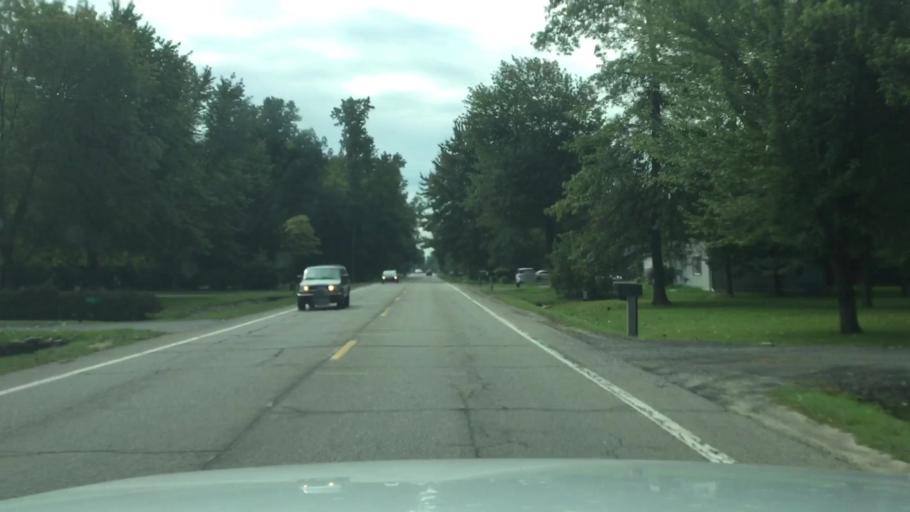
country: US
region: Michigan
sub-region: Wayne County
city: Belleville
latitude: 42.1672
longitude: -83.4826
